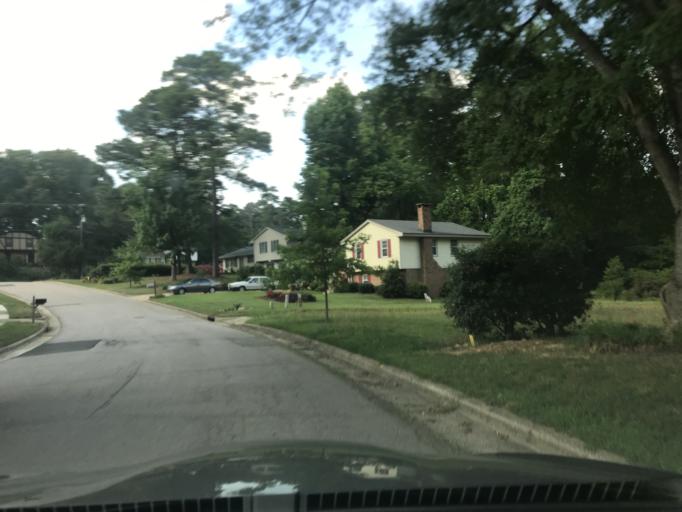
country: US
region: North Carolina
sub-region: Wake County
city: Raleigh
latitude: 35.8346
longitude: -78.5897
